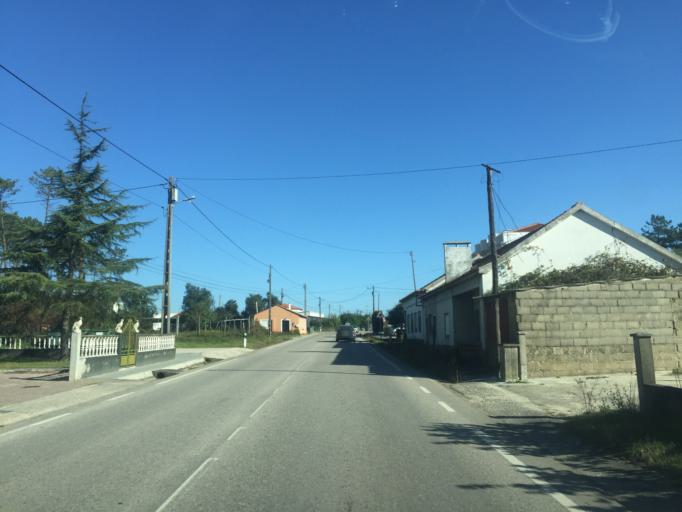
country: PT
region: Leiria
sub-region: Leiria
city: Monte Redondo
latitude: 39.9007
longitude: -8.8261
